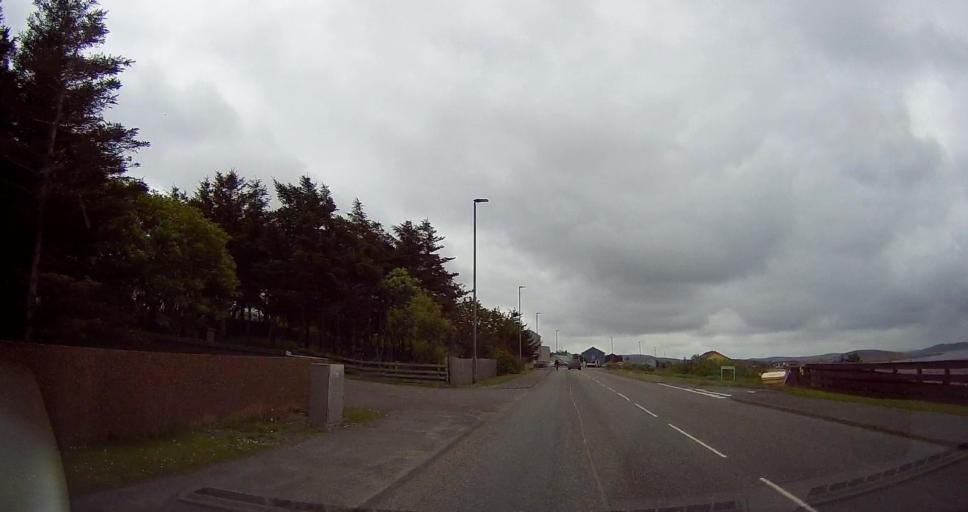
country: GB
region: Scotland
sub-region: Shetland Islands
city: Lerwick
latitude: 60.3934
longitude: -1.3505
